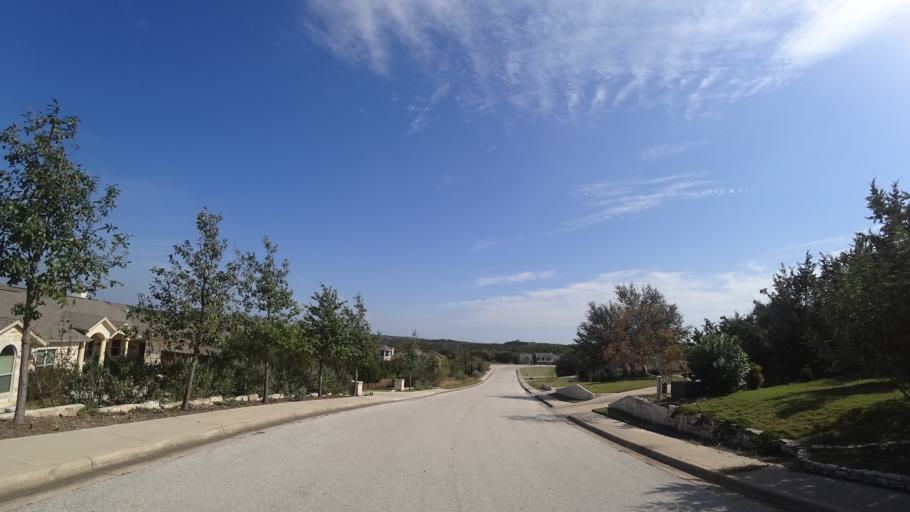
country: US
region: Texas
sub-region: Travis County
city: Bee Cave
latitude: 30.2240
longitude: -97.9344
